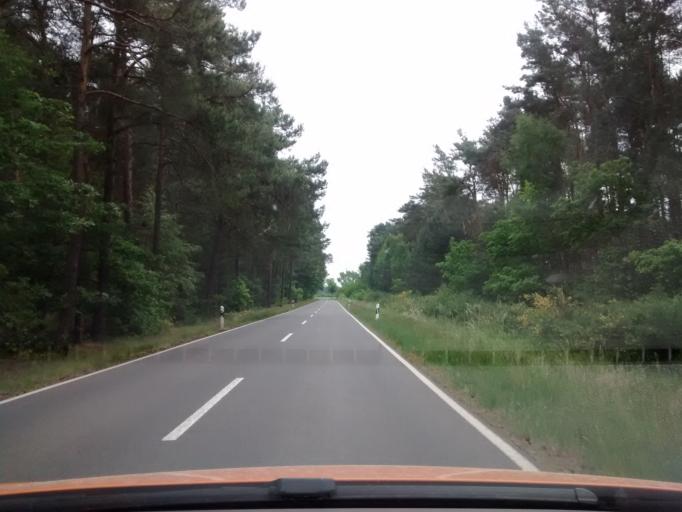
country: DE
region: Saxony-Anhalt
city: Holzdorf
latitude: 51.8345
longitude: 13.1847
